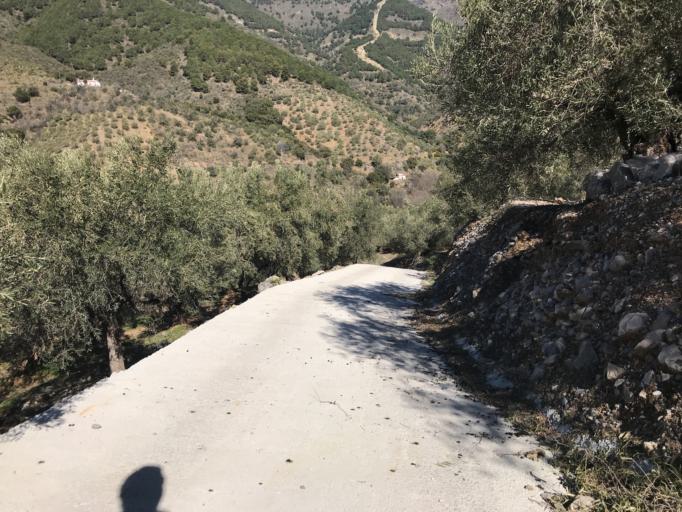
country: ES
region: Andalusia
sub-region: Provincia de Malaga
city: Canillas de Albaida
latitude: 36.8596
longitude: -3.9881
